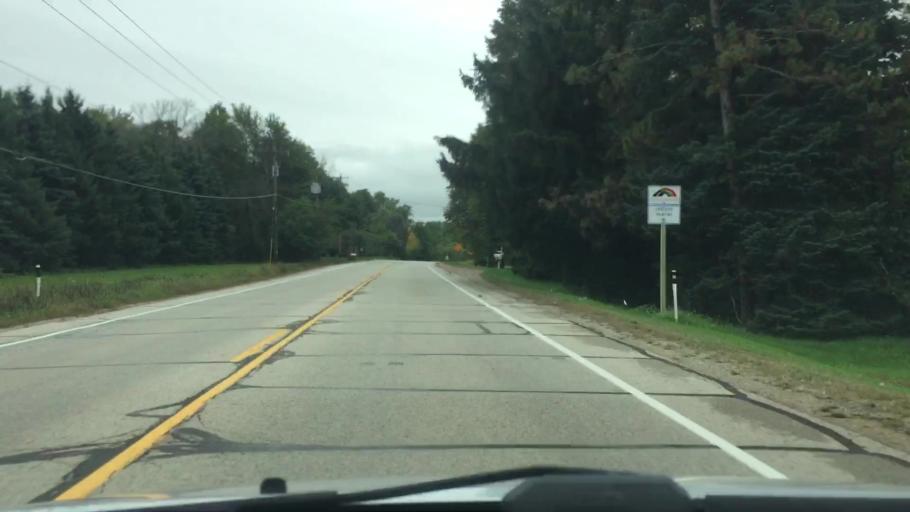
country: US
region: Wisconsin
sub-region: Walworth County
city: Elkhorn
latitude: 42.7701
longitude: -88.5553
